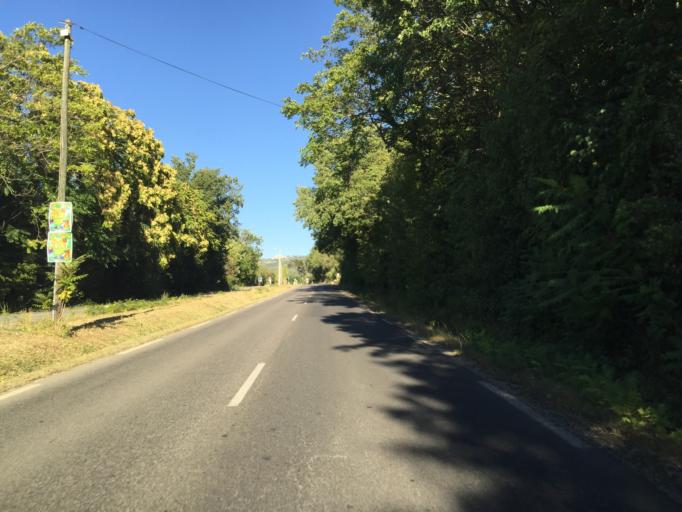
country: FR
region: Provence-Alpes-Cote d'Azur
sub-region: Departement du Vaucluse
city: Saignon
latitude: 43.8782
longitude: 5.4185
